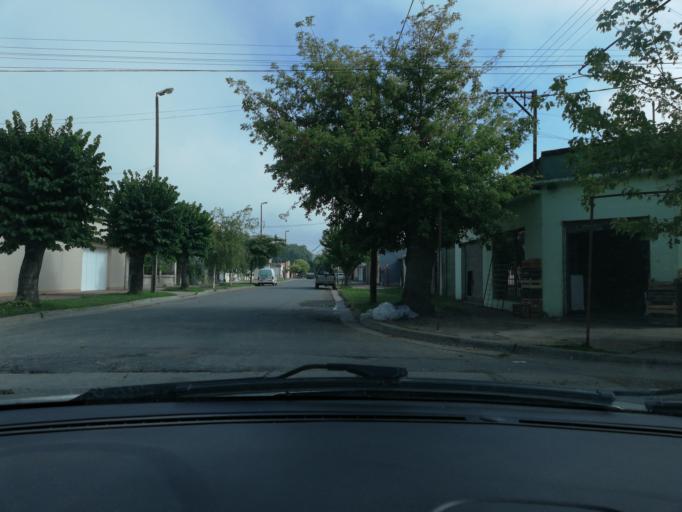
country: AR
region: Buenos Aires
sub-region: Partido de Balcarce
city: Balcarce
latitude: -37.8380
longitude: -58.2641
